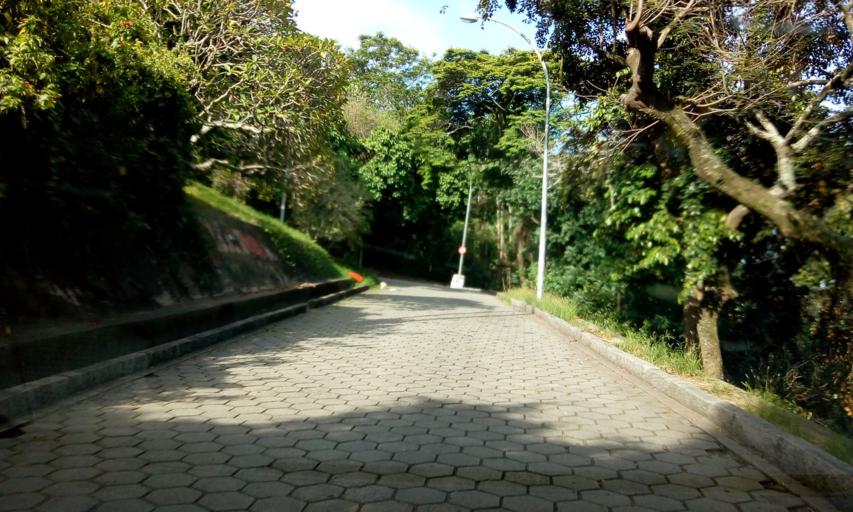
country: BR
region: Rio de Janeiro
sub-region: Rio De Janeiro
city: Rio de Janeiro
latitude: -22.9527
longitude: -43.1794
